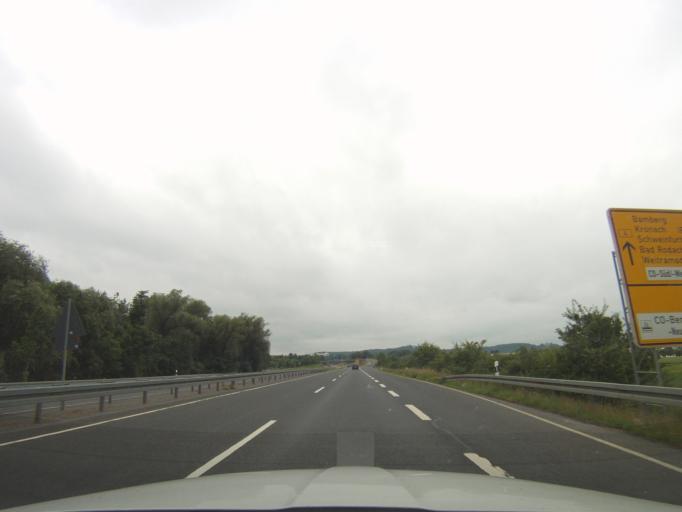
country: DE
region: Bavaria
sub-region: Upper Franconia
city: Coburg
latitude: 50.2815
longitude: 10.9650
